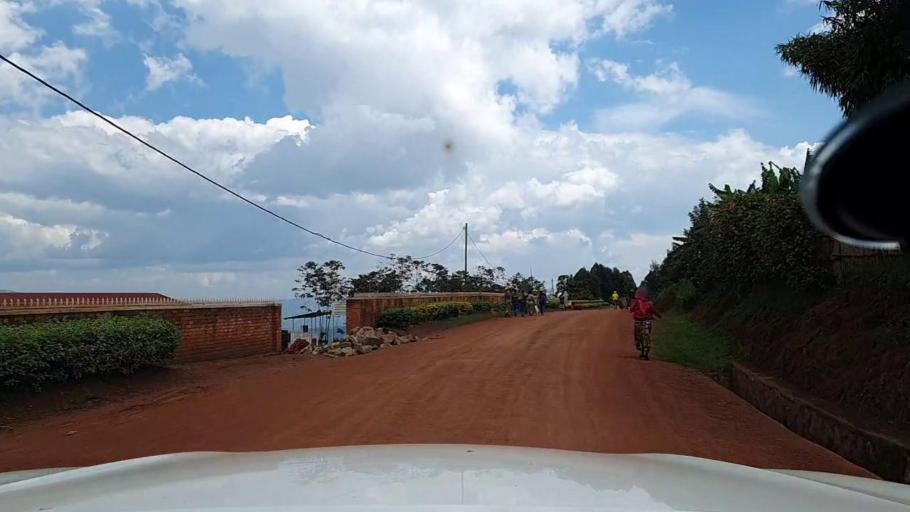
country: RW
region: Kigali
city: Kigali
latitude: -1.8110
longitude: 29.8450
